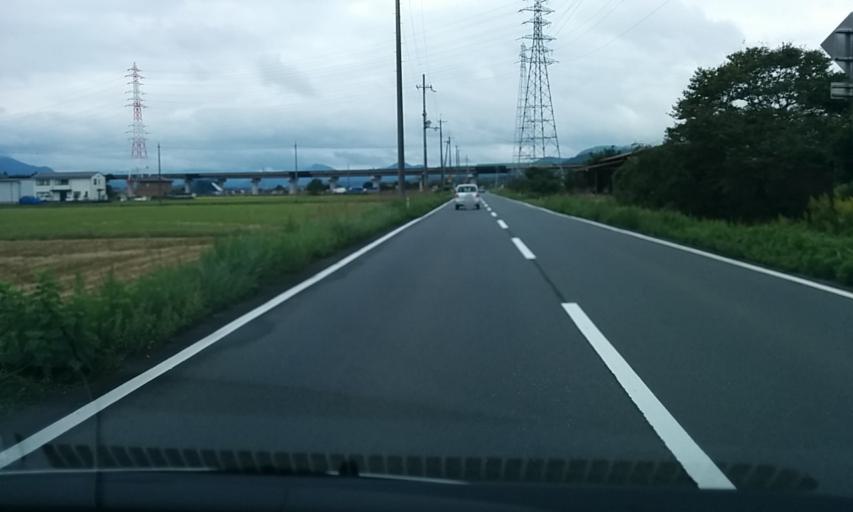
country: JP
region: Kyoto
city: Ayabe
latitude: 35.3064
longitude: 135.1962
